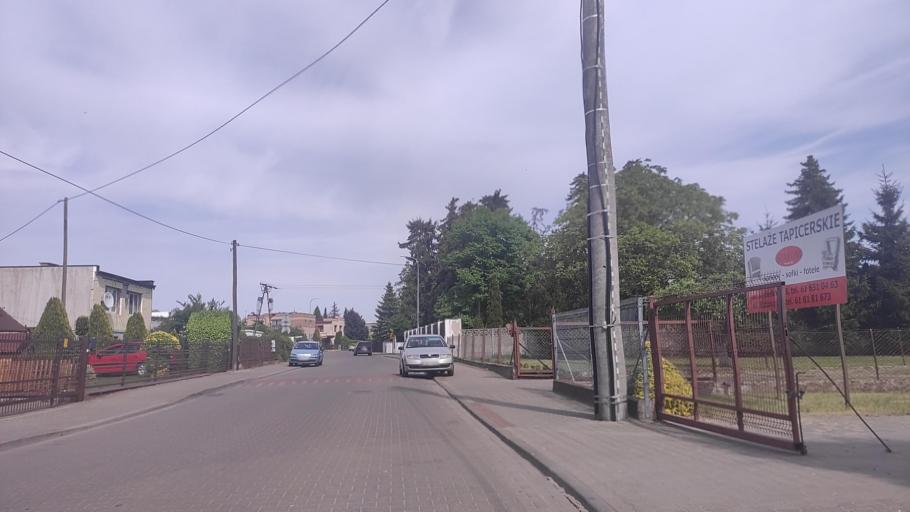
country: PL
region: Greater Poland Voivodeship
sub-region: Powiat poznanski
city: Swarzedz
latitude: 52.4082
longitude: 17.0876
